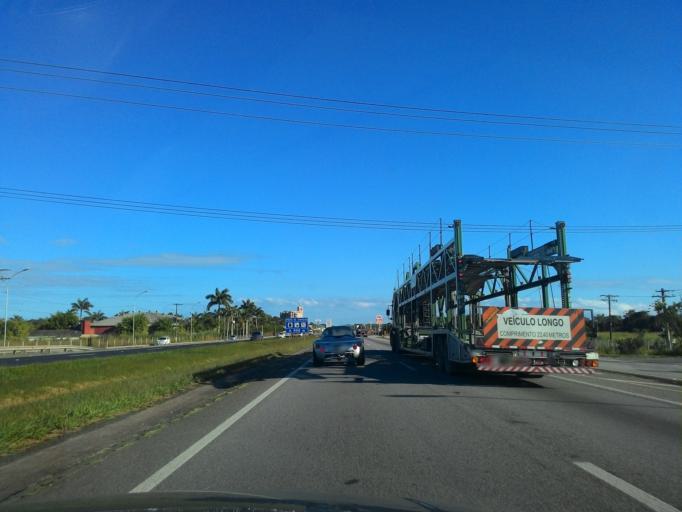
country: BR
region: Sao Paulo
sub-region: Registro
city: Registro
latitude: -24.5213
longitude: -47.8540
